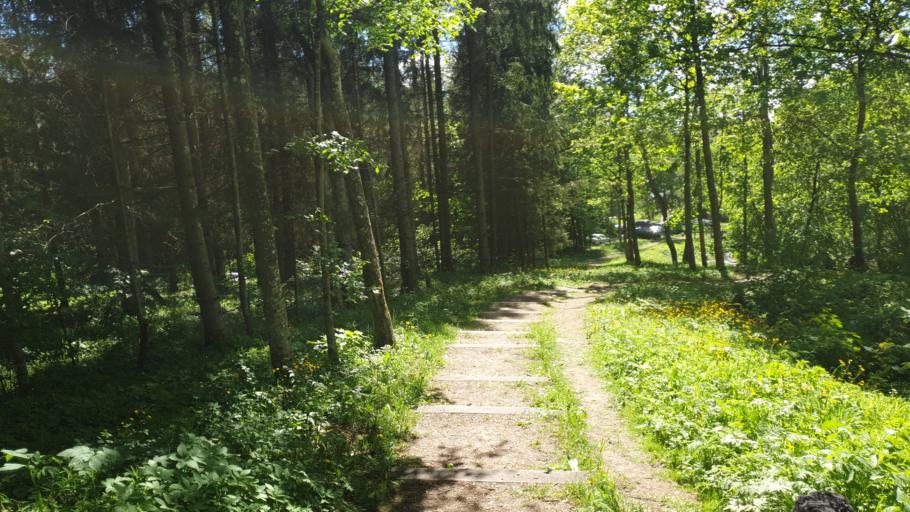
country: LT
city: Moletai
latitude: 55.0718
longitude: 25.4146
